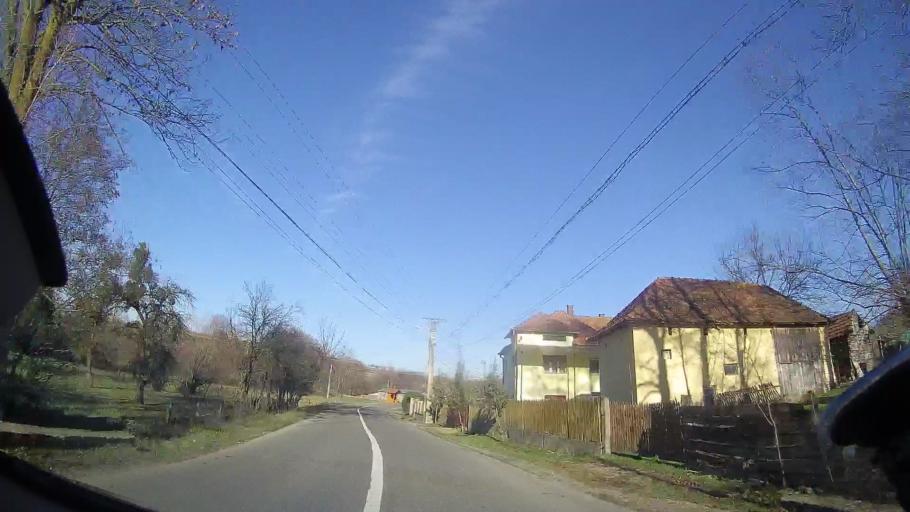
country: RO
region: Bihor
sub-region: Comuna Bratca
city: Bratca
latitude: 46.9413
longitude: 22.6046
